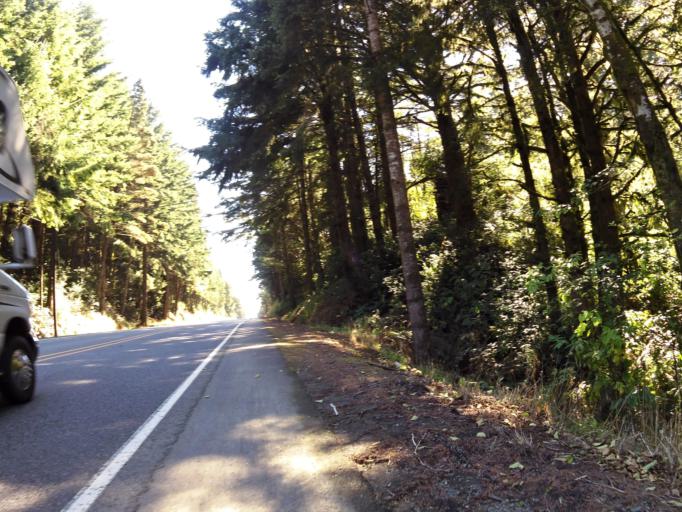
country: US
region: Oregon
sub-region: Curry County
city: Port Orford
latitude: 42.7346
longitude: -124.4725
